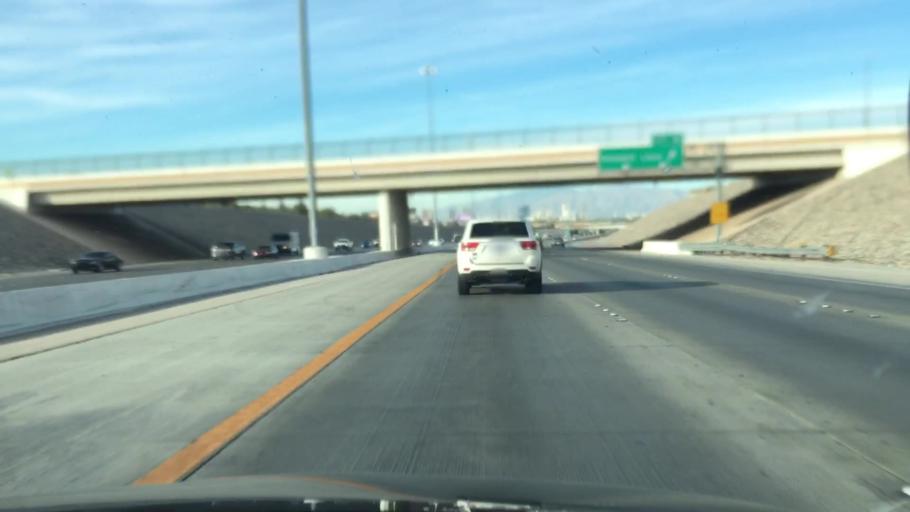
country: US
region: Nevada
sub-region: Clark County
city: Whitney
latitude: 36.0346
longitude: -115.1328
